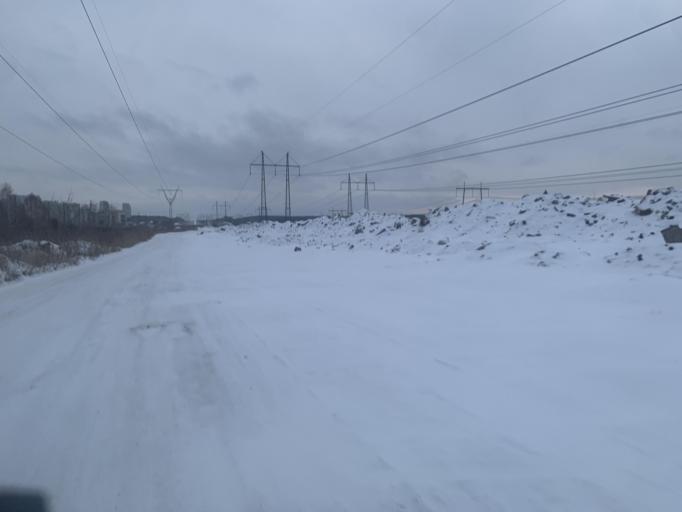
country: RU
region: Chelyabinsk
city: Roshchino
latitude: 55.1874
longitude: 61.2579
